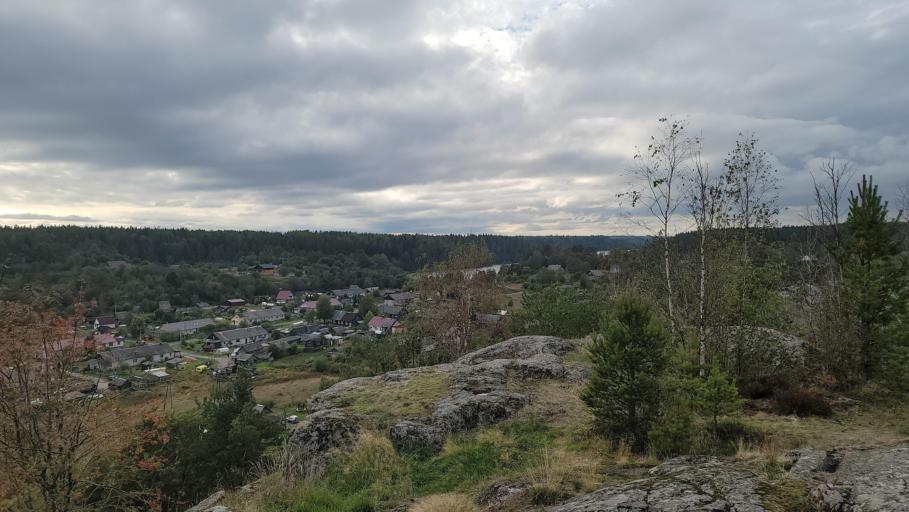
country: RU
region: Leningrad
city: Kuznechnoye
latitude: 61.2377
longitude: 29.6841
